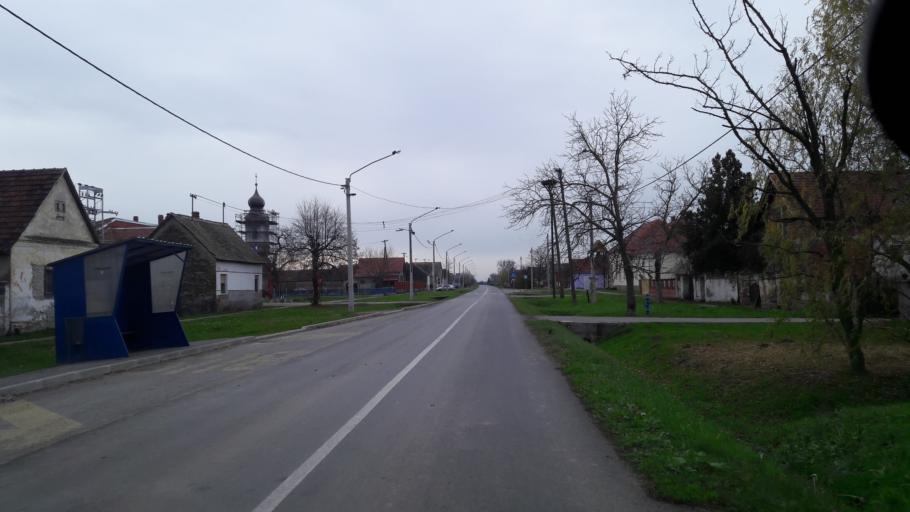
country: HR
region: Osjecko-Baranjska
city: Vladislavci
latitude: 45.4519
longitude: 18.5585
